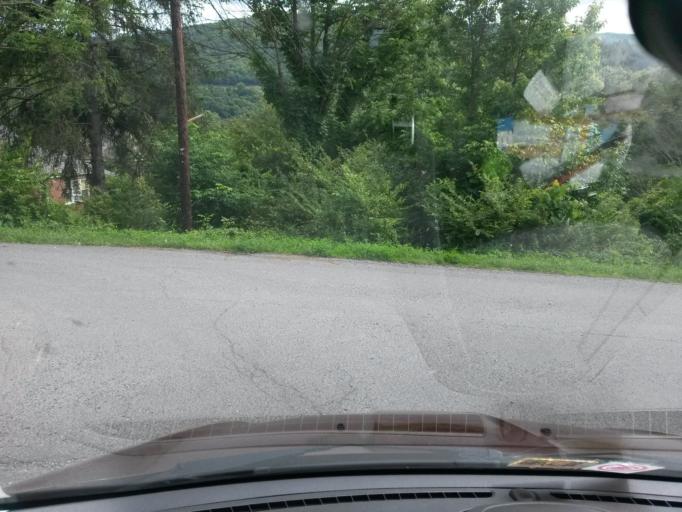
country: US
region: Virginia
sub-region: Alleghany County
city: Clifton Forge
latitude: 37.8186
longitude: -79.8294
